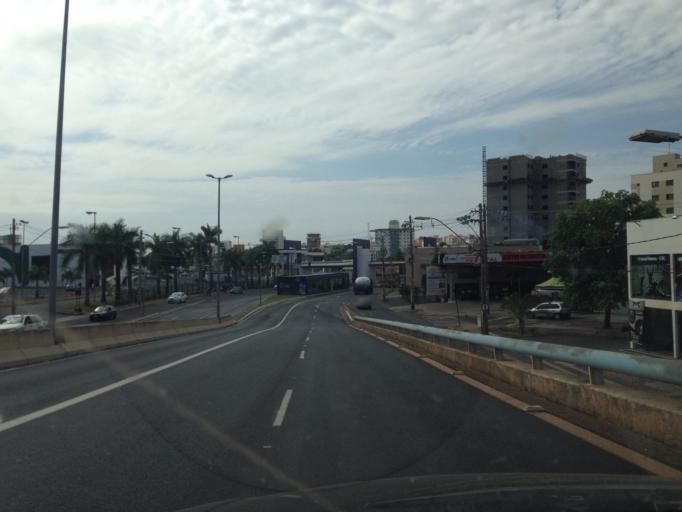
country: BR
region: Minas Gerais
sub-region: Uberlandia
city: Uberlandia
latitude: -18.9116
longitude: -48.2614
